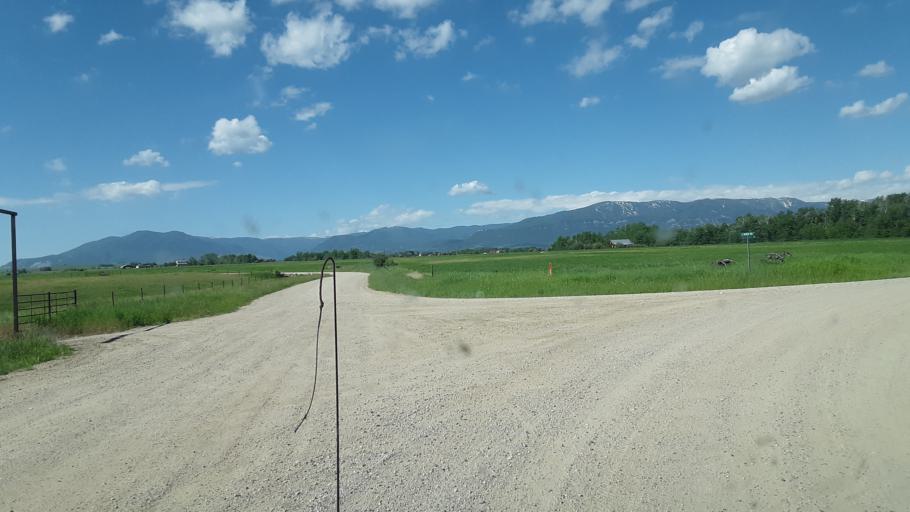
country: US
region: Montana
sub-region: Carbon County
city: Red Lodge
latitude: 45.2787
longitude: -109.1932
